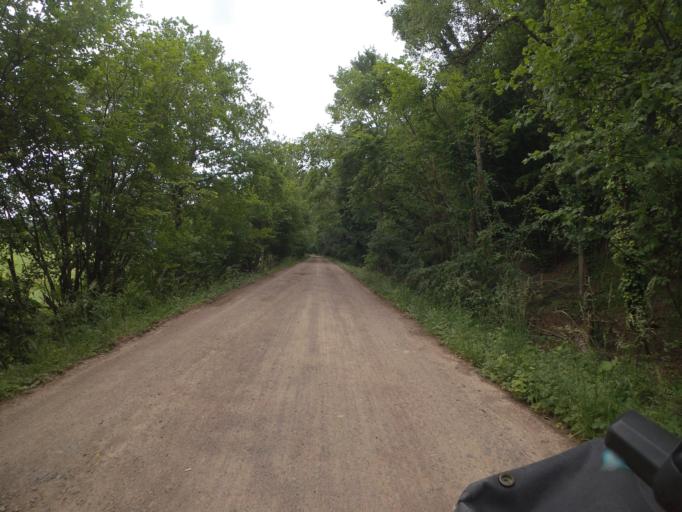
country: DE
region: Rheinland-Pfalz
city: Huffelsheim
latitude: 49.8061
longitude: 7.8020
